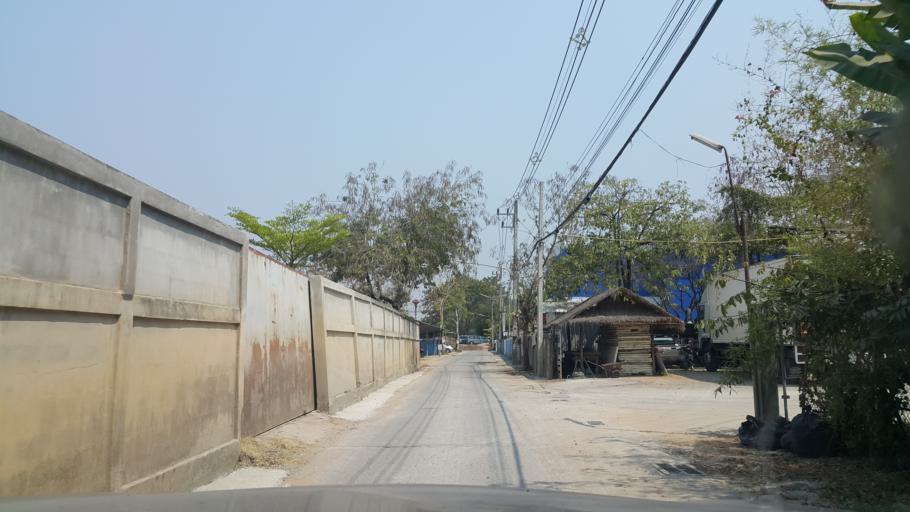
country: TH
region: Chiang Mai
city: Saraphi
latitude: 18.7509
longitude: 99.0304
